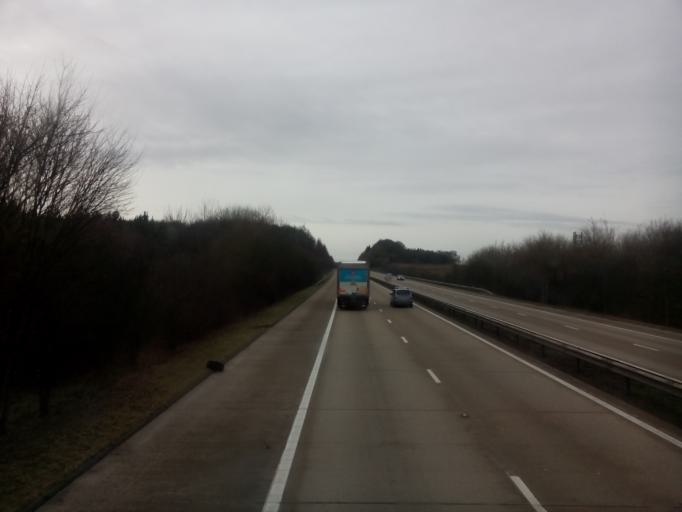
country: GB
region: England
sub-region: Hampshire
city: Kings Worthy
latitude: 51.1351
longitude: -1.2470
